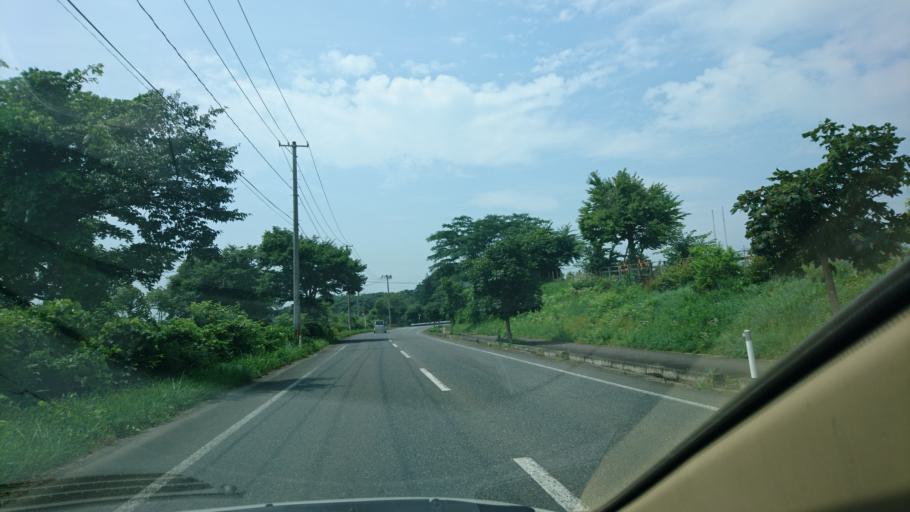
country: JP
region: Iwate
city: Kitakami
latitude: 39.2569
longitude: 141.0844
